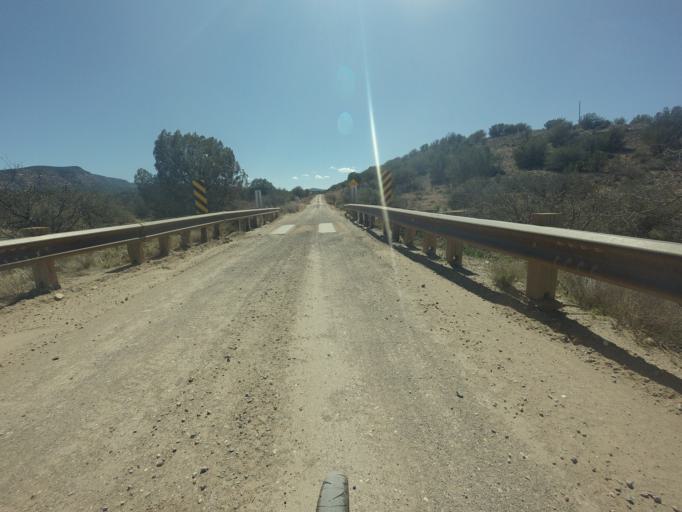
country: US
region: Arizona
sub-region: Yavapai County
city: Lake Montezuma
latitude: 34.6413
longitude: -111.7194
